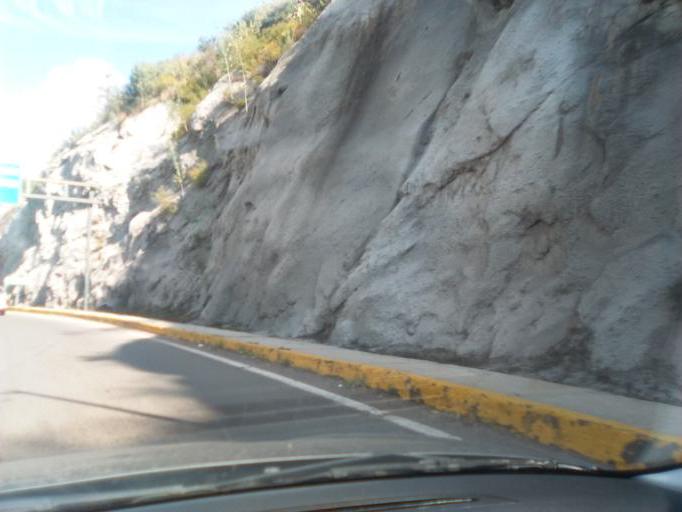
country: MX
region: Guanajuato
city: Guanajuato
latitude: 21.0092
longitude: -101.2686
